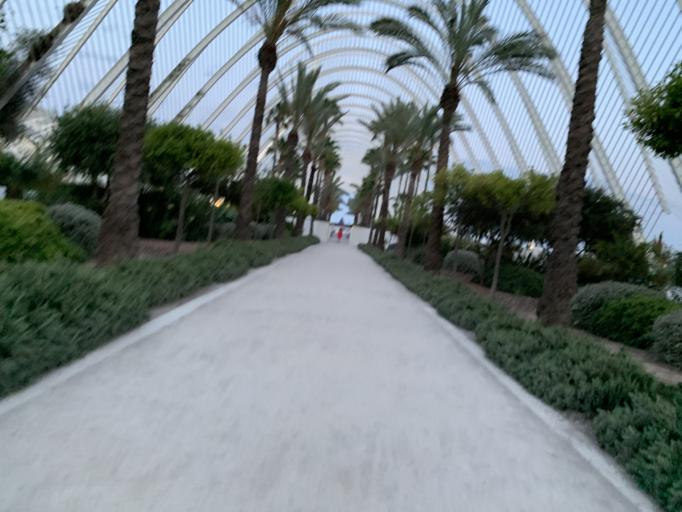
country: ES
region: Valencia
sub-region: Provincia de Valencia
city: Valencia
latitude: 39.4557
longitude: -0.3543
